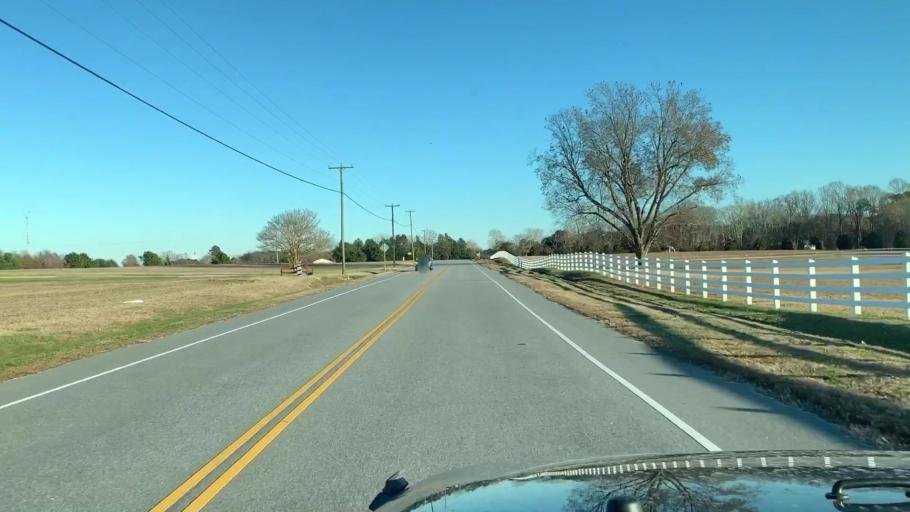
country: US
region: Virginia
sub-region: James City County
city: Williamsburg
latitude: 37.3847
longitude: -76.8153
